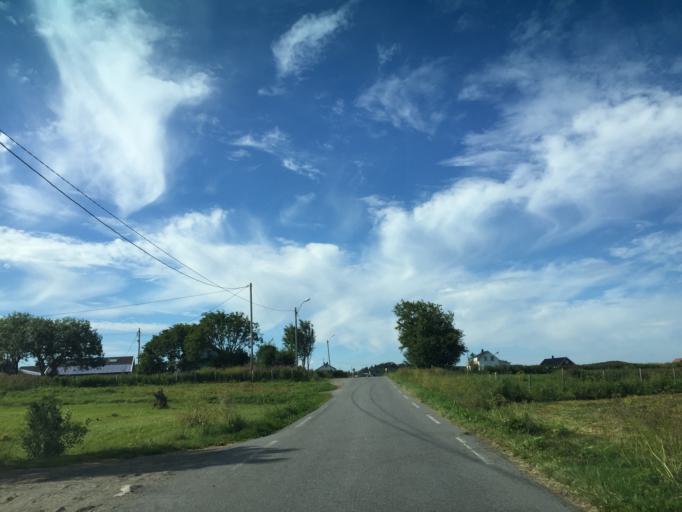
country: NO
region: Nordland
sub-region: Vagan
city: Kabelvag
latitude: 68.3935
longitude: 14.4701
